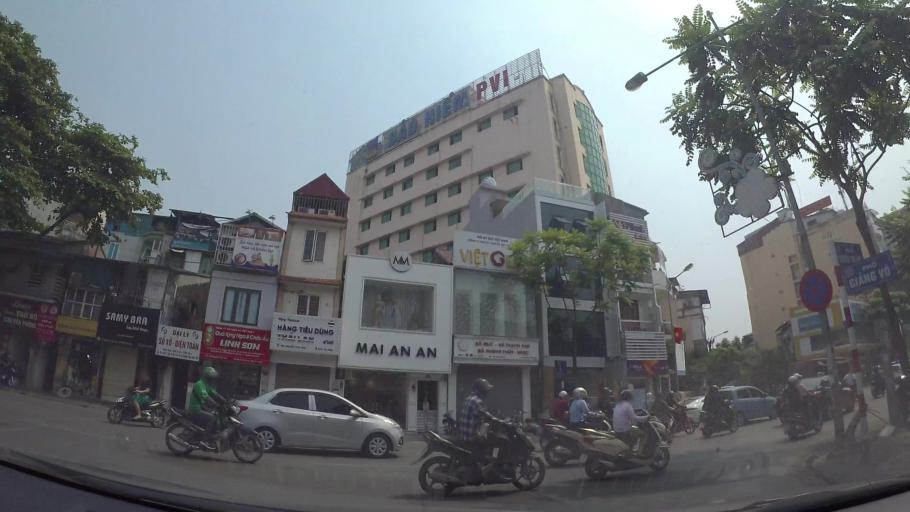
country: VN
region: Ha Noi
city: Dong Da
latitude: 21.0320
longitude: 105.8299
